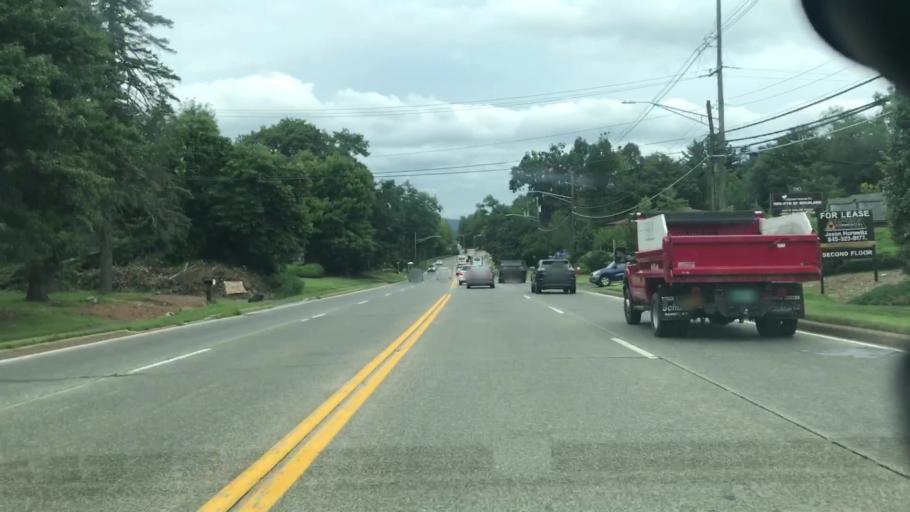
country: US
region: New York
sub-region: Rockland County
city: New City
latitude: 41.1295
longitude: -73.9916
